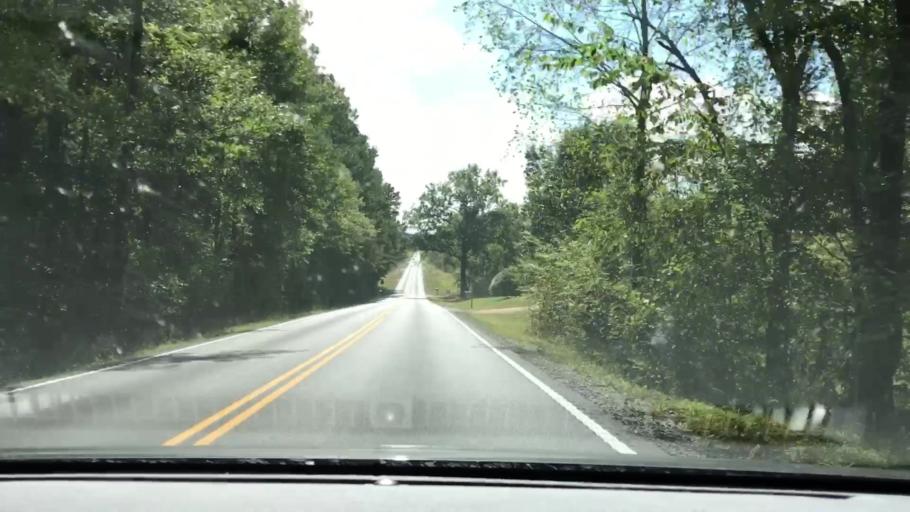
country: US
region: Kentucky
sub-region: Graves County
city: Mayfield
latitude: 36.8671
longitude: -88.5737
